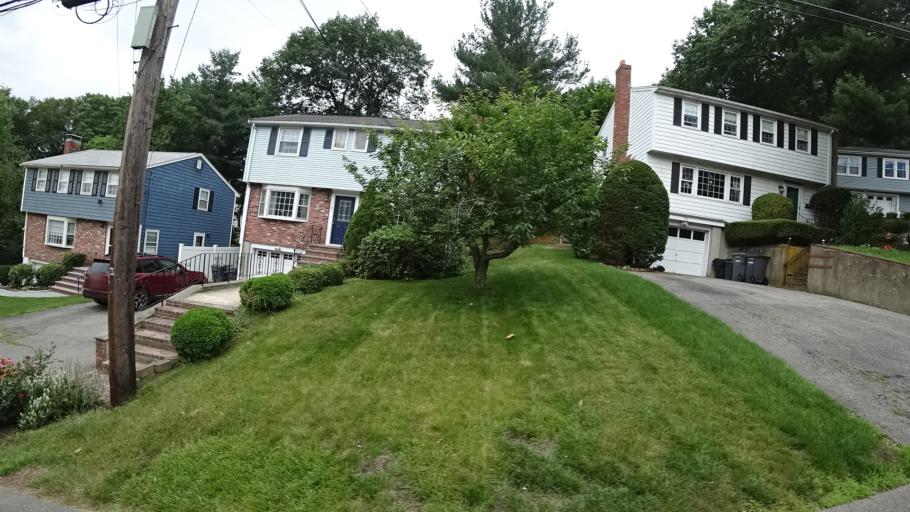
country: US
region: Massachusetts
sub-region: Norfolk County
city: Dedham
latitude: 42.2263
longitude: -71.1521
